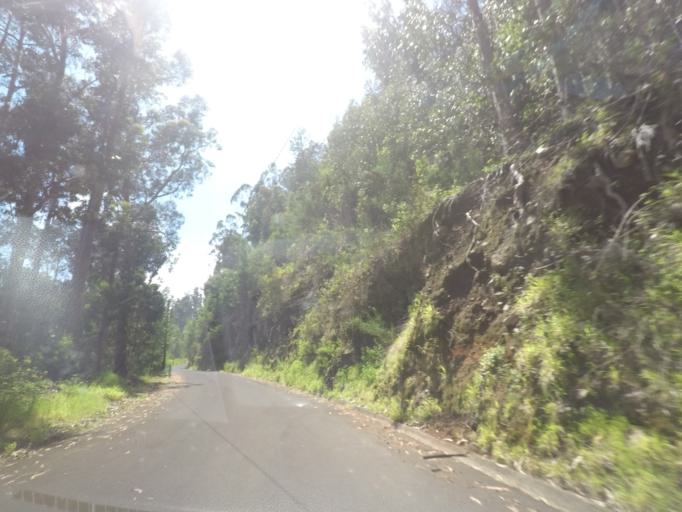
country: PT
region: Madeira
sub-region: Calheta
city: Arco da Calheta
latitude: 32.7298
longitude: -17.1295
